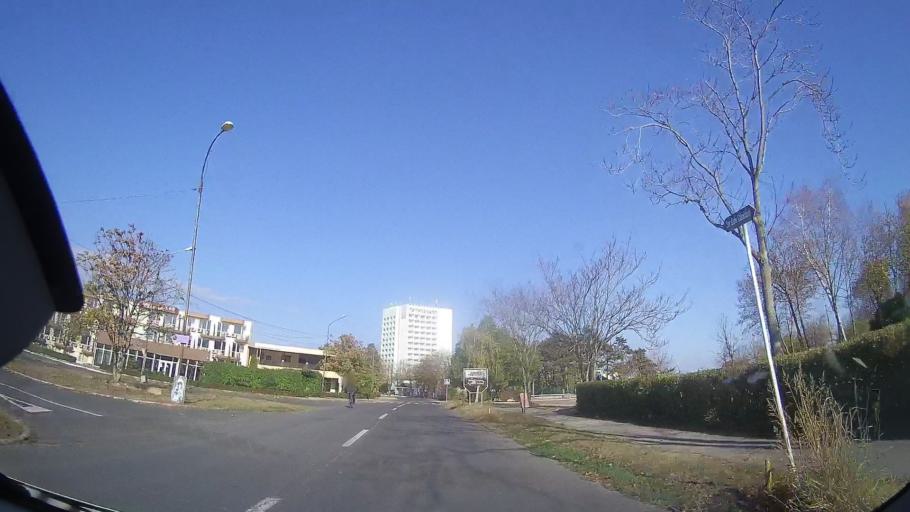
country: RO
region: Constanta
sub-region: Municipiul Mangalia
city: Mangalia
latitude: 43.8526
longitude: 28.6060
